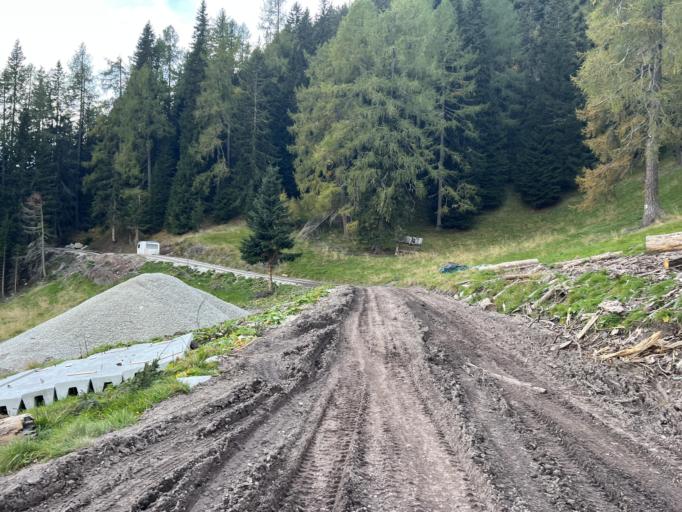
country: IT
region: Veneto
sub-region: Provincia di Belluno
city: Granvilla
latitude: 46.6321
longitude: 12.6969
